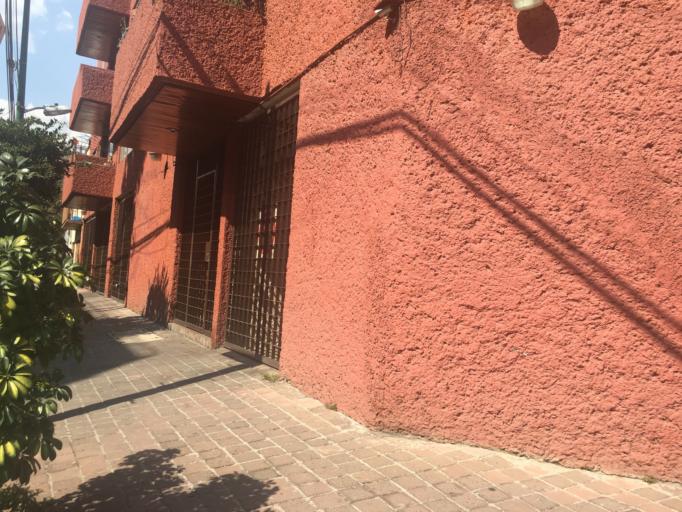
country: MX
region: Mexico City
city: Coyoacan
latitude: 19.3594
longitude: -99.1452
